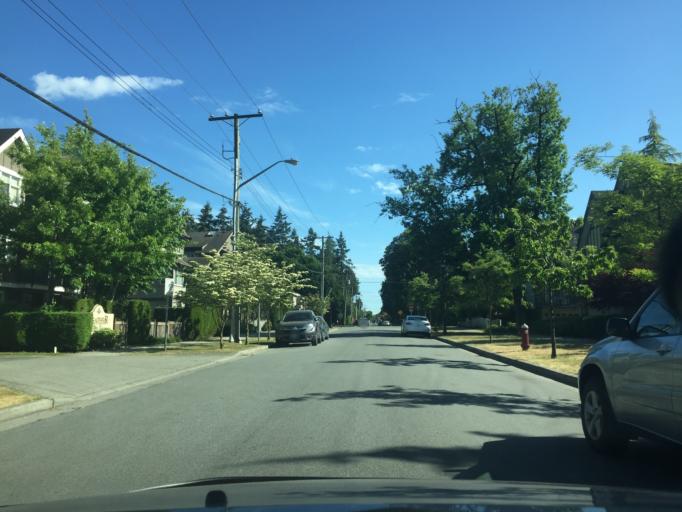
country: CA
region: British Columbia
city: Richmond
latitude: 49.1600
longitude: -123.1227
